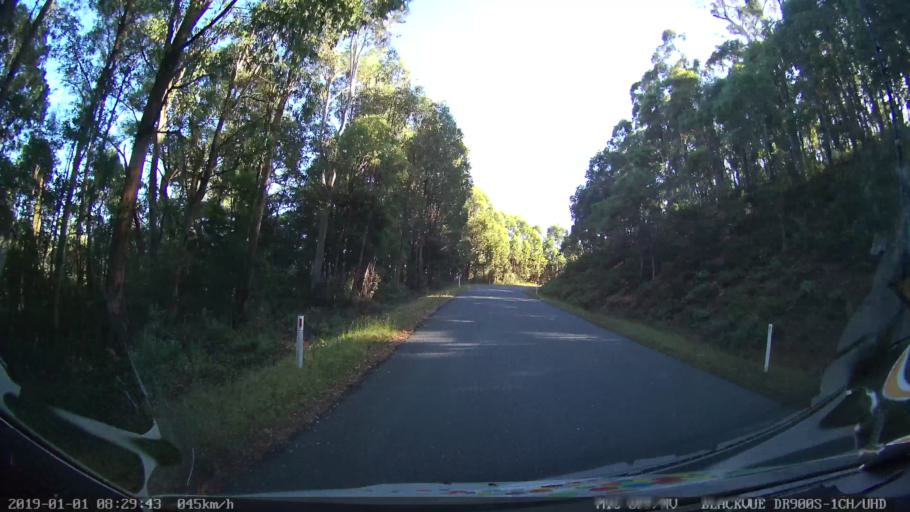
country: AU
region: New South Wales
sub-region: Snowy River
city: Jindabyne
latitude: -36.3758
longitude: 148.1941
